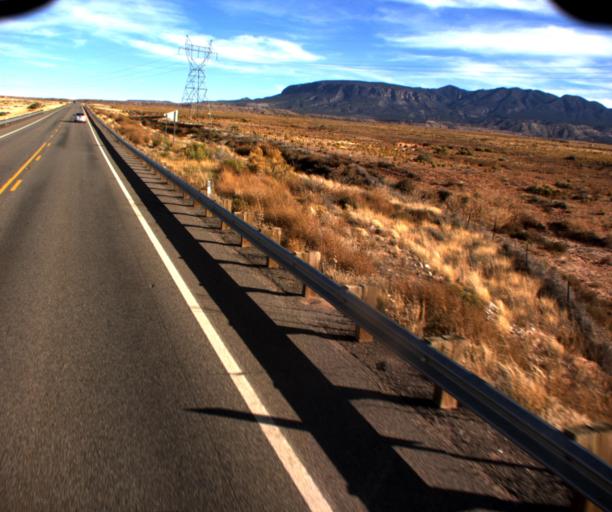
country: US
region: Arizona
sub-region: Apache County
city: Lukachukai
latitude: 36.9378
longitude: -109.2424
